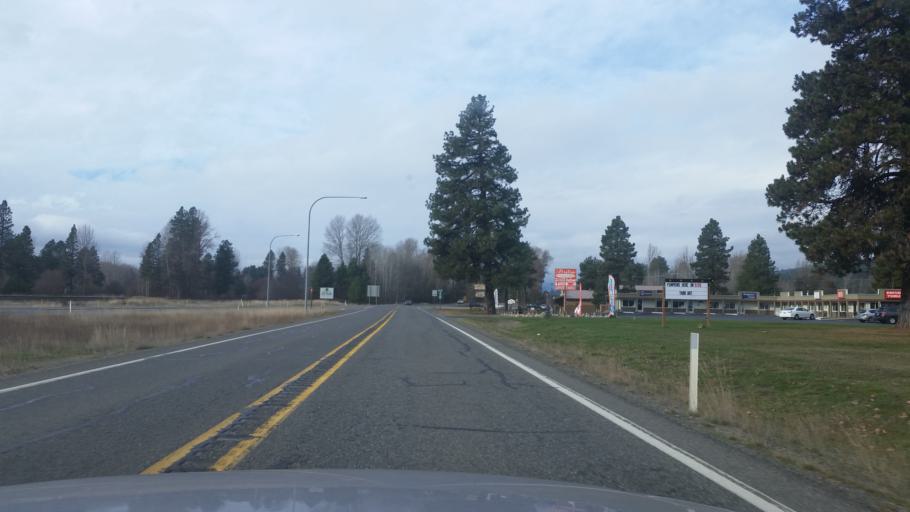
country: US
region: Washington
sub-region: Kittitas County
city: Cle Elum
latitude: 47.1884
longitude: -120.9020
